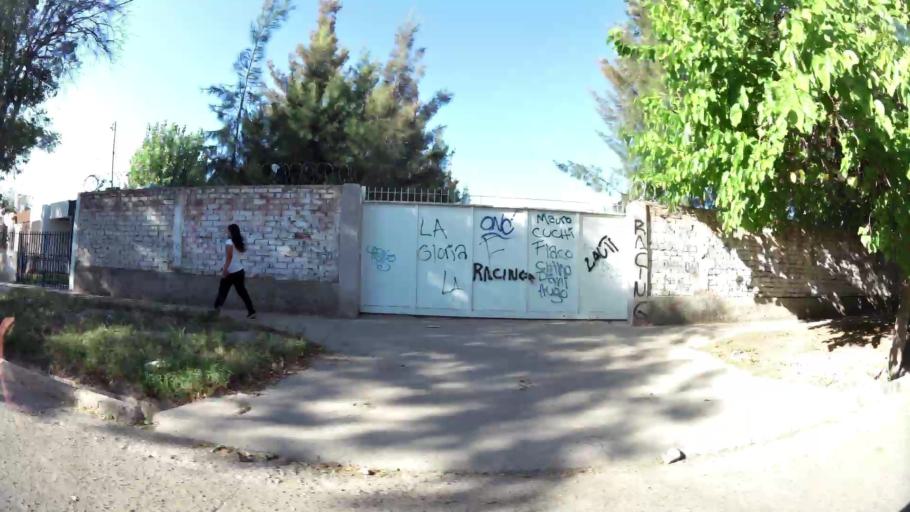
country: AR
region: Mendoza
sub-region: Departamento de Godoy Cruz
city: Godoy Cruz
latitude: -32.9383
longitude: -68.8349
